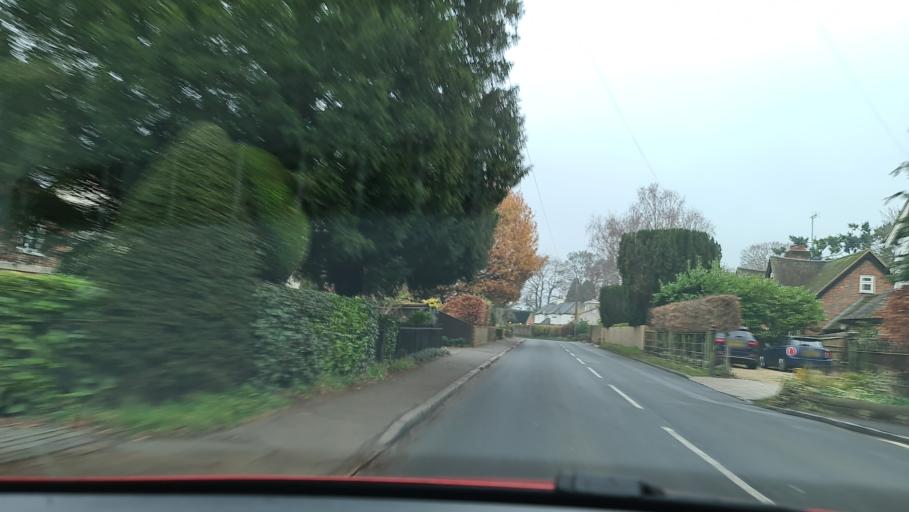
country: GB
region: England
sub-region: Buckinghamshire
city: Beaconsfield
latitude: 51.6323
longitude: -0.6891
